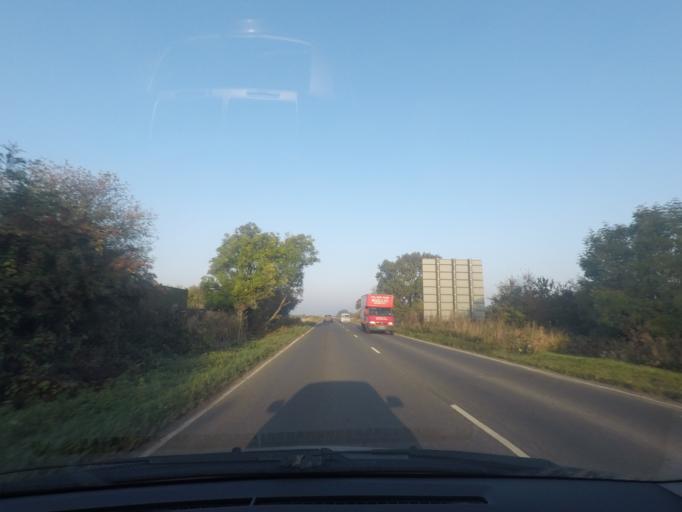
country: GB
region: England
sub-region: City of York
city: Nether Poppleton
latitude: 53.9827
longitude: -1.2073
